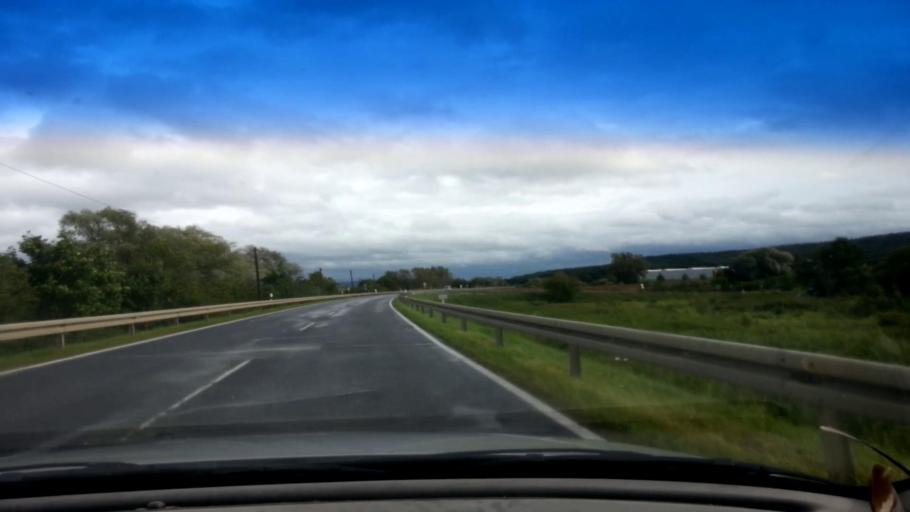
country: DE
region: Bavaria
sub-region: Upper Franconia
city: Pettstadt
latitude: 49.8353
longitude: 10.9341
